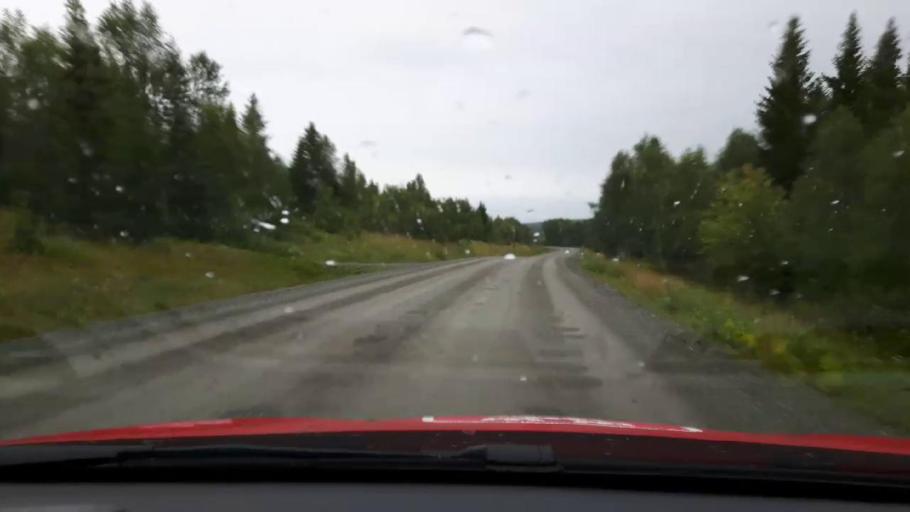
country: SE
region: Jaemtland
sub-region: Are Kommun
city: Are
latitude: 63.4568
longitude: 12.6423
